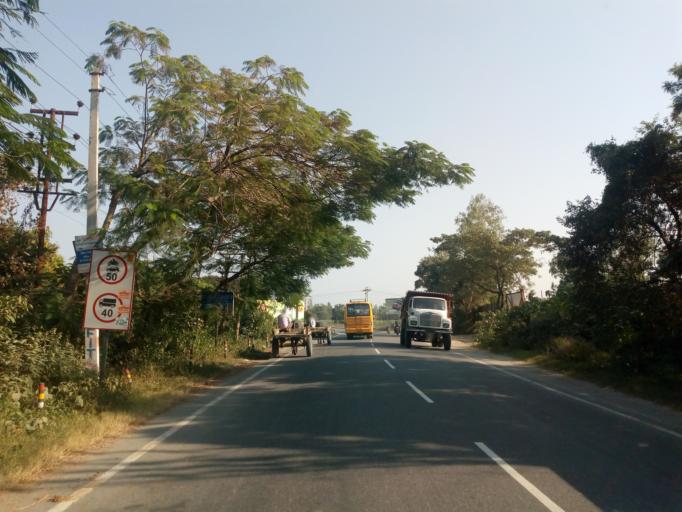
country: IN
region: Uttarakhand
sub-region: Dehradun
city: Harbatpur
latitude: 30.4201
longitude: 77.7790
